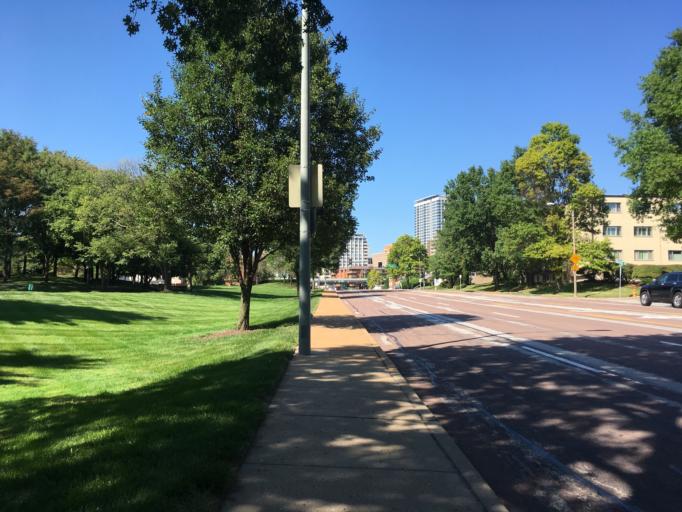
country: US
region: Missouri
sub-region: Saint Louis County
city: Clayton
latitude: 38.6427
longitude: -90.3439
